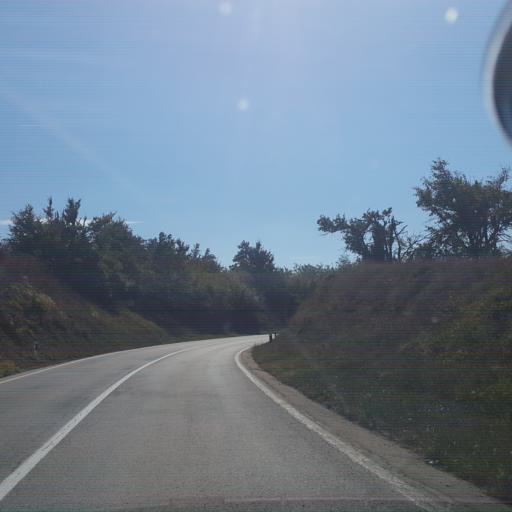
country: RS
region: Central Serbia
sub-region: Zajecarski Okrug
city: Knjazevac
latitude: 43.4791
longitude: 22.2307
